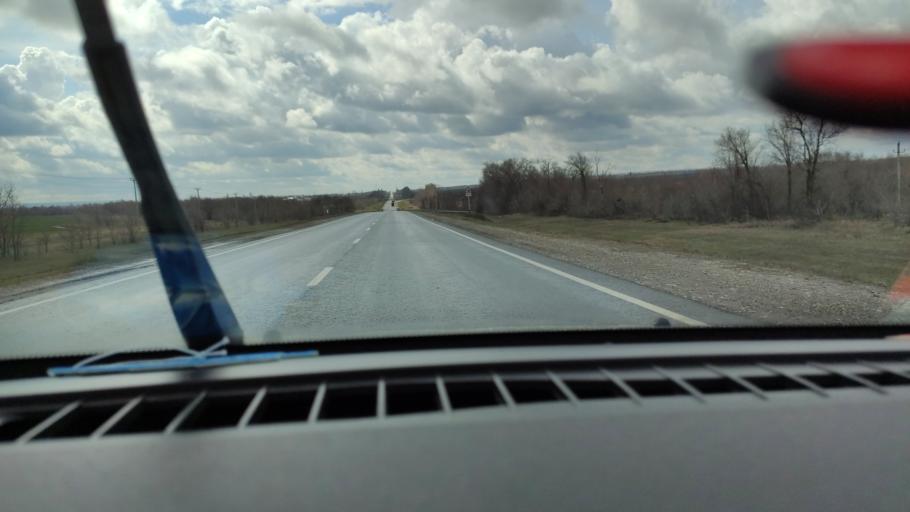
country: RU
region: Samara
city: Yelkhovka
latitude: 53.8975
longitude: 50.2690
